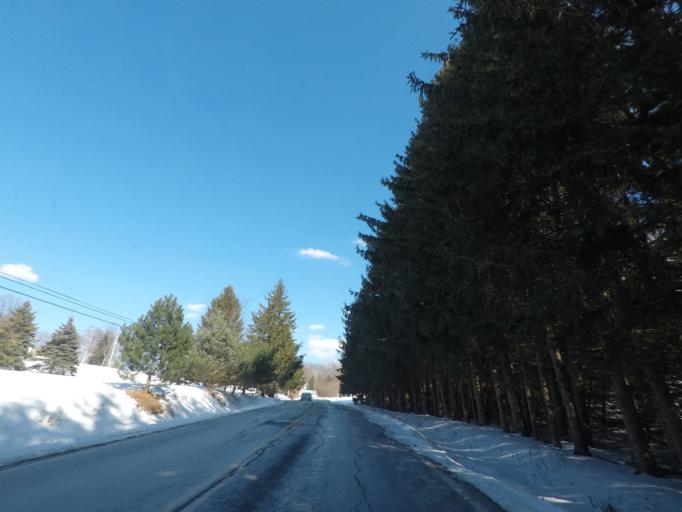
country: US
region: New York
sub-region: Saratoga County
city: Waterford
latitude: 42.7947
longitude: -73.6194
